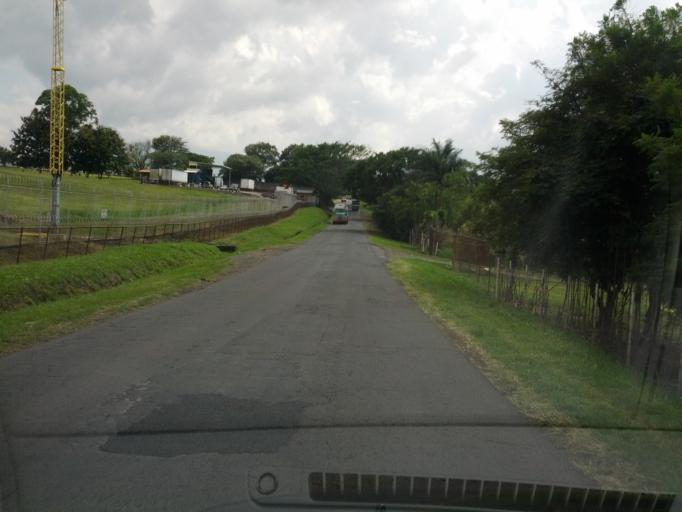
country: CR
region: Alajuela
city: Alajuela
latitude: 9.9889
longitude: -84.2238
